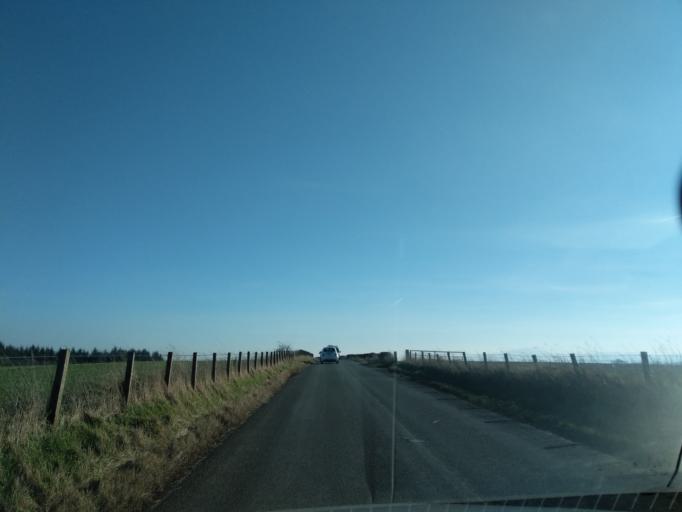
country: GB
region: Scotland
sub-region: South Lanarkshire
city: Carluke
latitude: 55.6874
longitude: -3.8286
